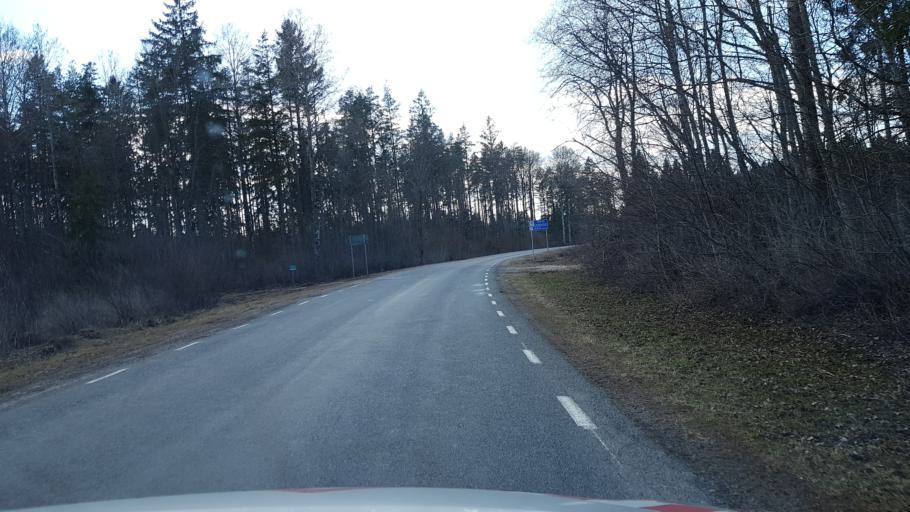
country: EE
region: Laeaene-Virumaa
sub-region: Tapa vald
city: Tapa
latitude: 59.1812
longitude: 26.0096
